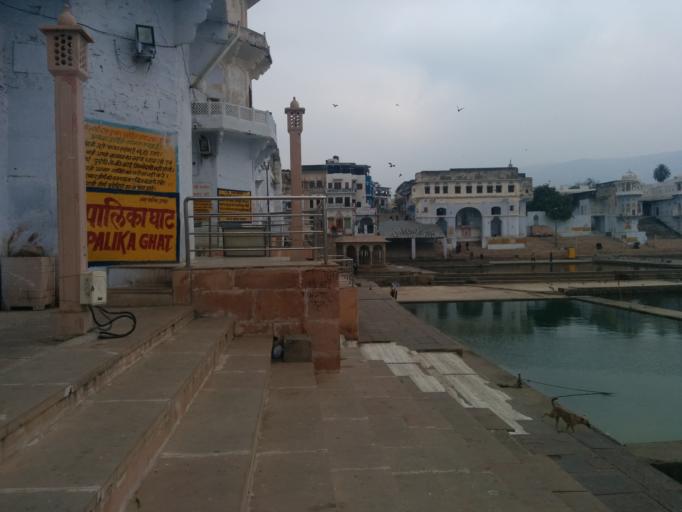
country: IN
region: Rajasthan
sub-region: Ajmer
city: Pushkar
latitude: 26.4894
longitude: 74.5547
